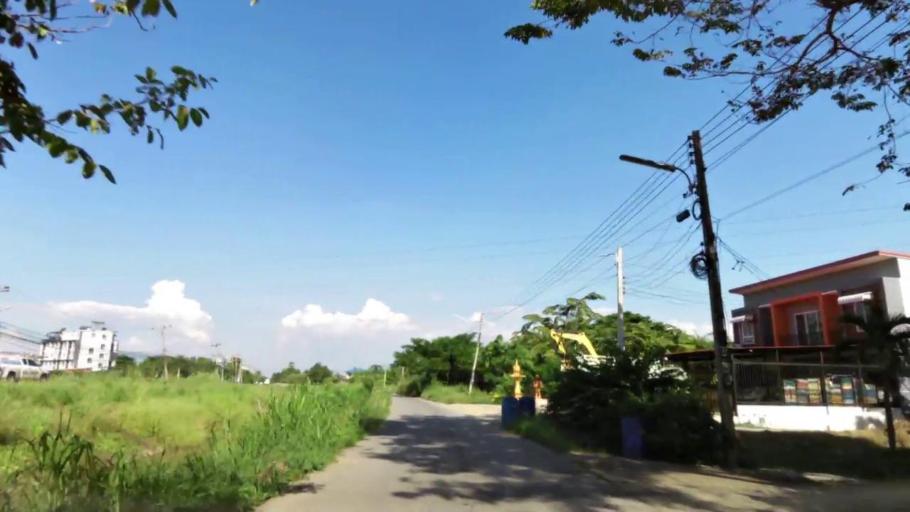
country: TH
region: Ang Thong
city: Ang Thong
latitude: 14.5858
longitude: 100.4652
